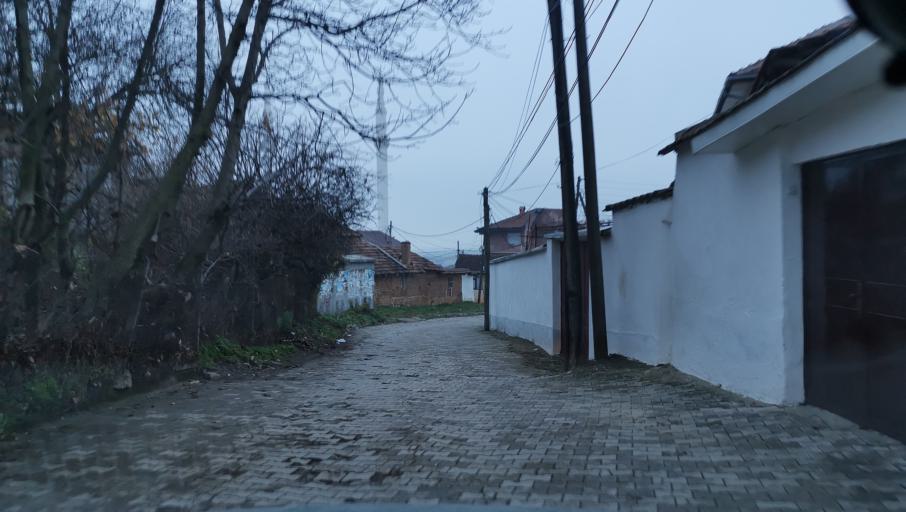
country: MK
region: Debar
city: Debar
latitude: 41.5276
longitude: 20.5281
